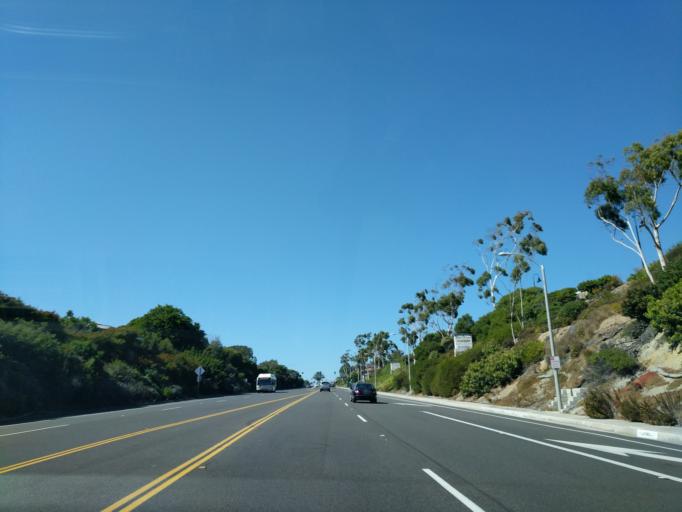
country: US
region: California
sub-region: Orange County
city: Dana Point
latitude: 33.4837
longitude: -117.7235
